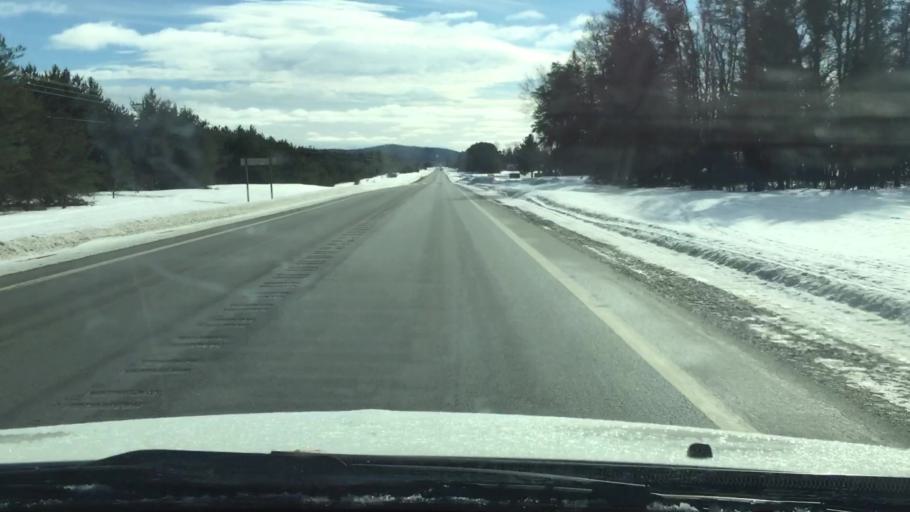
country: US
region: Michigan
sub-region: Antrim County
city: Mancelona
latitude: 44.9299
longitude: -85.0509
